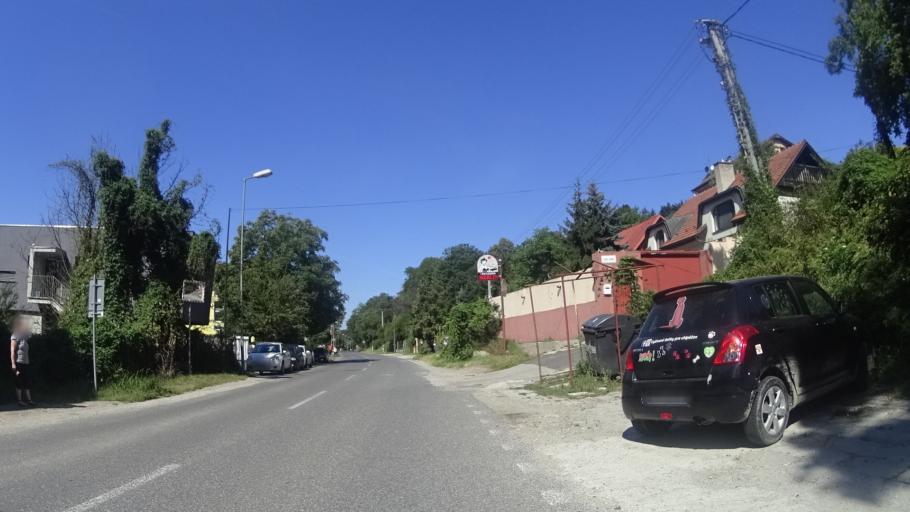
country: AT
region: Lower Austria
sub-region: Politischer Bezirk Bruck an der Leitha
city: Wolfsthal
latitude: 48.1516
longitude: 17.0330
